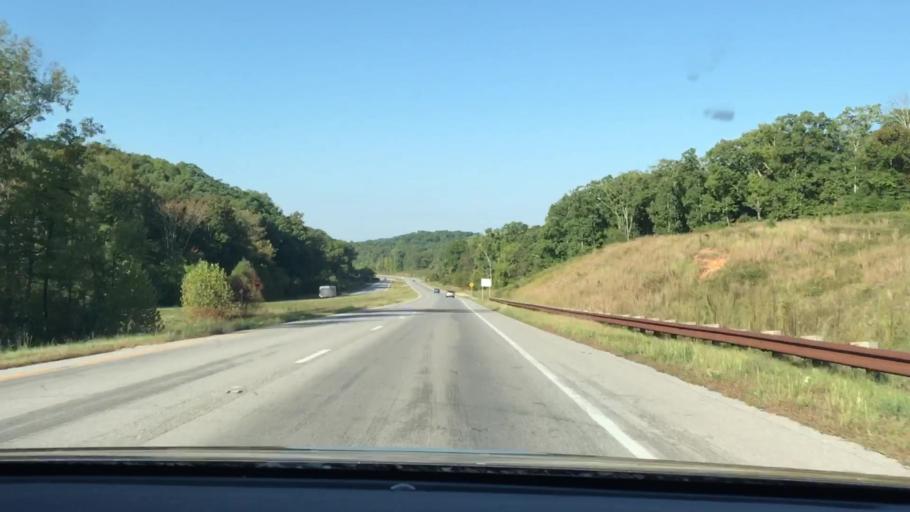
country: US
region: Kentucky
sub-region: Trigg County
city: Cadiz
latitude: 36.7796
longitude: -88.0895
